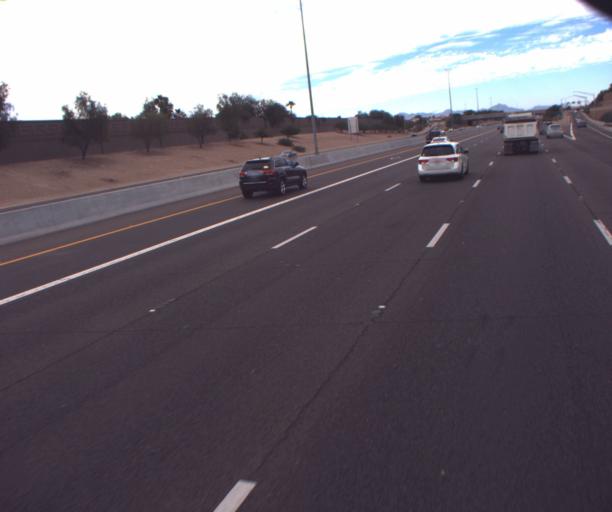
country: US
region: Arizona
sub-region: Maricopa County
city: Chandler
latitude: 33.2874
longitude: -111.8697
